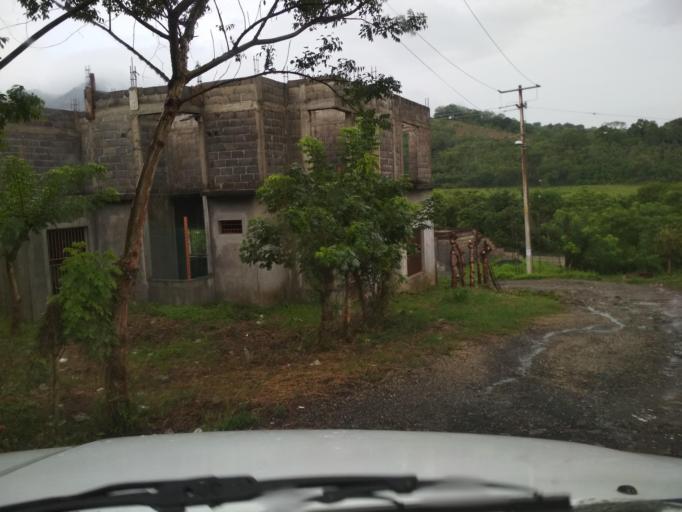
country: MX
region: Veracruz
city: Santiago Tuxtla
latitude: 18.4527
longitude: -95.3137
